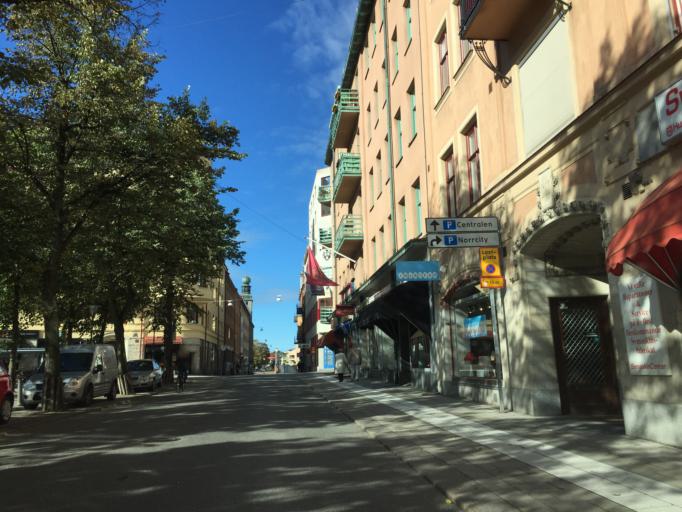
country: SE
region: OErebro
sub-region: Orebro Kommun
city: Orebro
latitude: 59.2755
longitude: 15.2135
